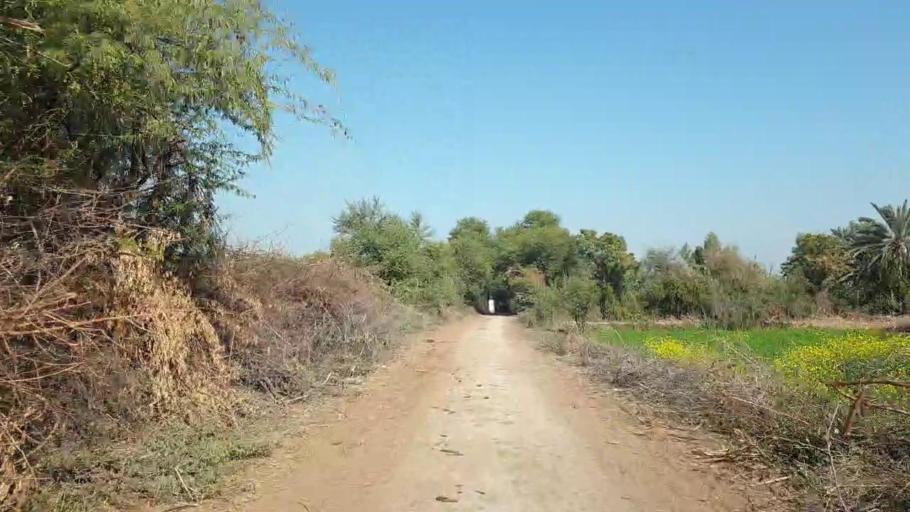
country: PK
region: Sindh
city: Shahpur Chakar
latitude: 26.0617
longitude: 68.4821
